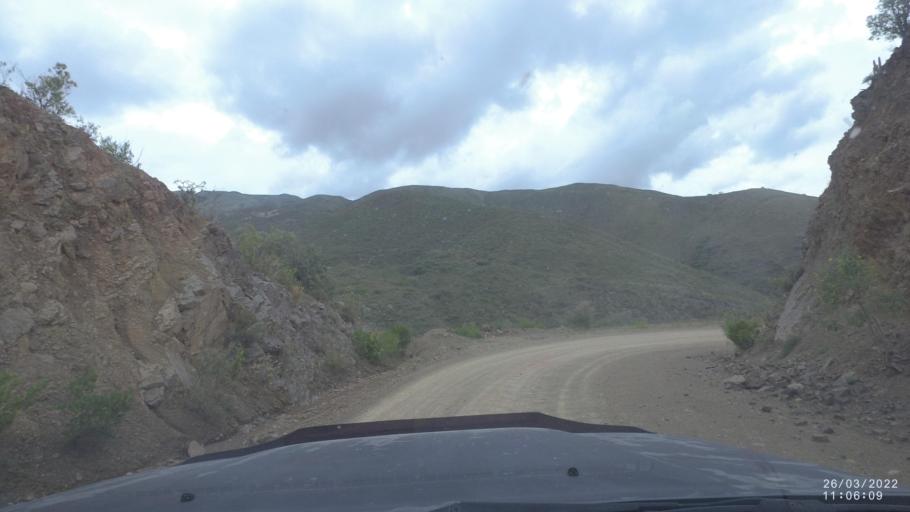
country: BO
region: Cochabamba
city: Tarata
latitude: -17.5320
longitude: -66.0188
